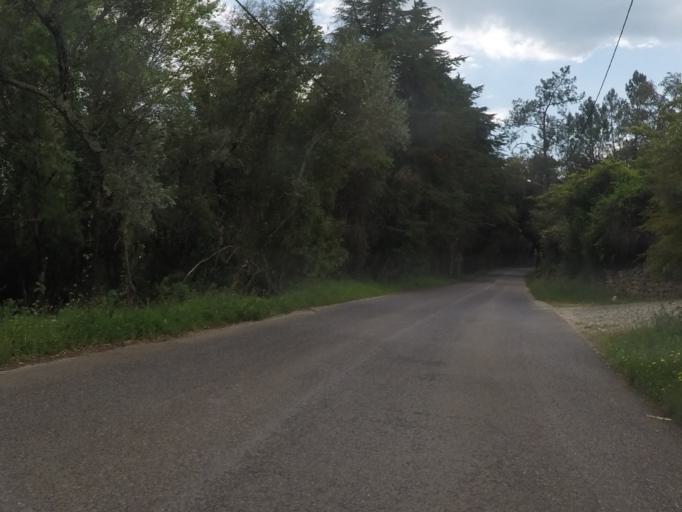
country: PT
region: Setubal
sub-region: Palmela
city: Quinta do Anjo
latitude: 38.5041
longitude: -8.9829
